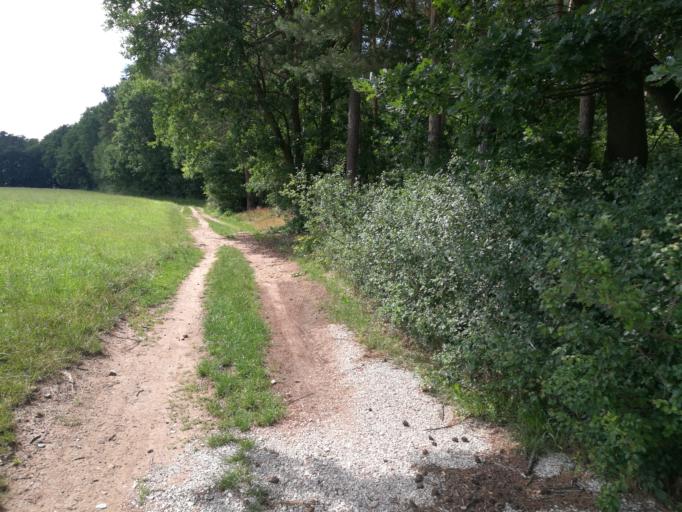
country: DE
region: Bavaria
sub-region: Regierungsbezirk Mittelfranken
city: Seukendorf
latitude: 49.4938
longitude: 10.8992
